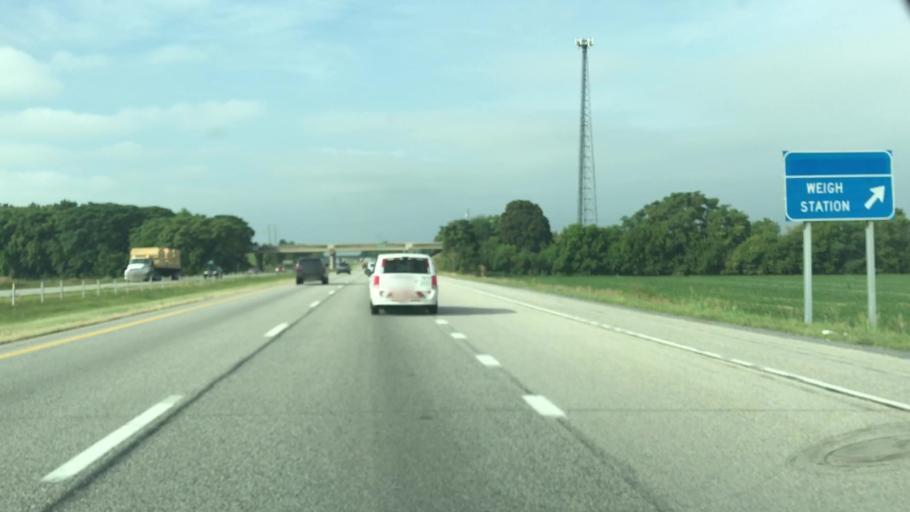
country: US
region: Pennsylvania
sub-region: Franklin County
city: Guilford Siding
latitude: 39.8718
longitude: -77.6801
